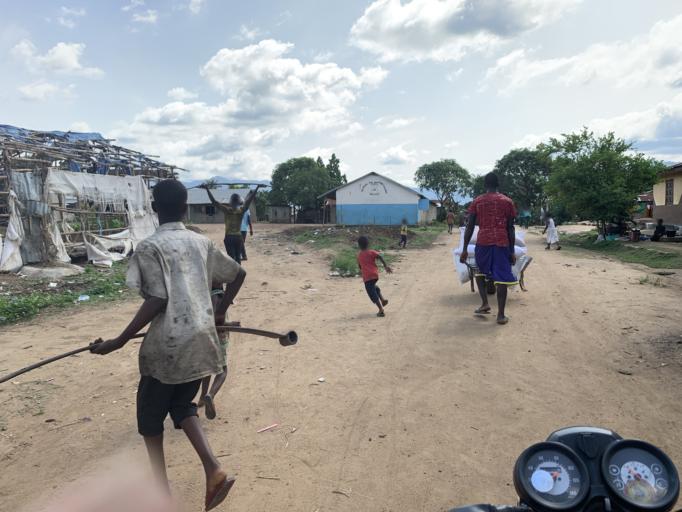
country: SL
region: Western Area
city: Waterloo
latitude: 8.3323
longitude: -13.0493
